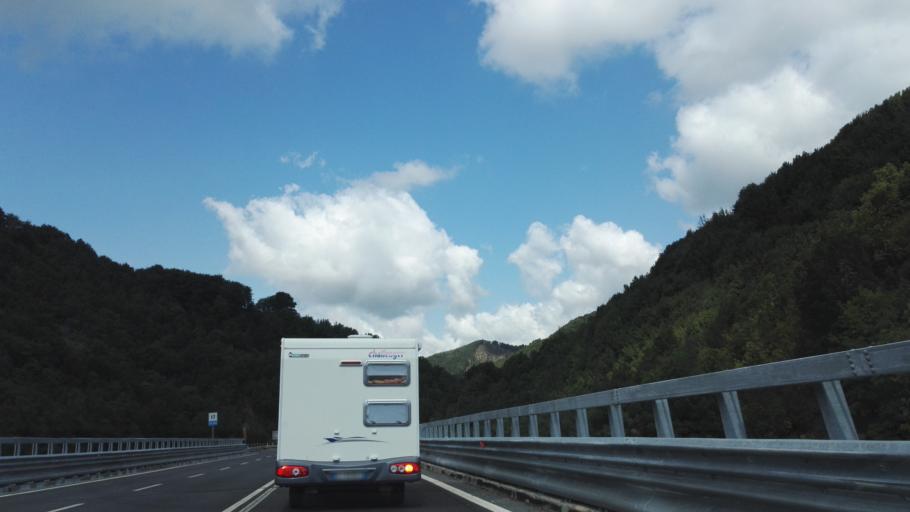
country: IT
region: Calabria
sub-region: Provincia di Reggio Calabria
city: Amato
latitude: 38.4064
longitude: 16.1504
